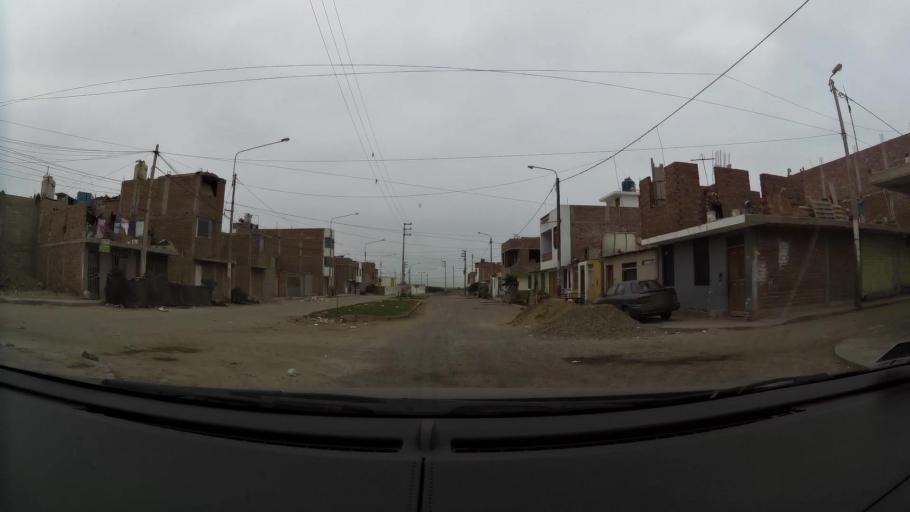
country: PE
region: La Libertad
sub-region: Provincia de Trujillo
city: Buenos Aires
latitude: -8.1494
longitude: -79.0461
